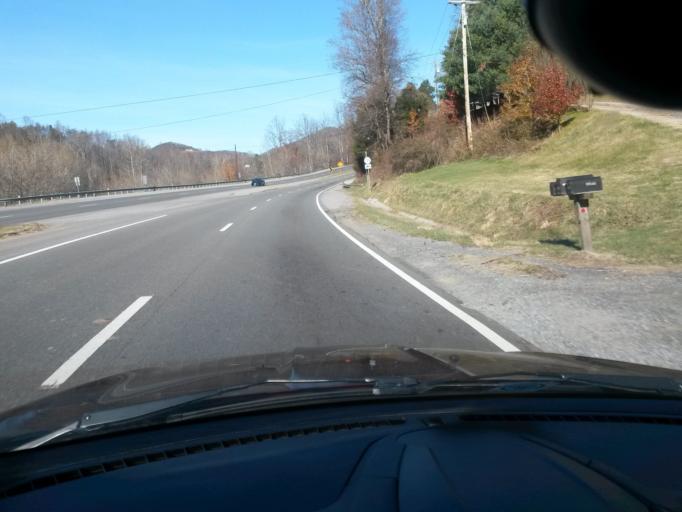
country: US
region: Virginia
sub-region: Roanoke County
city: Narrows
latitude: 37.1714
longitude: -79.9421
